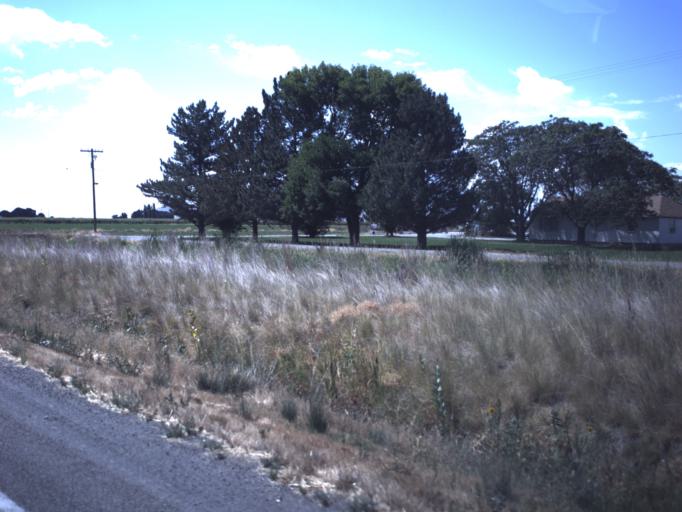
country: US
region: Utah
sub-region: Box Elder County
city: Elwood
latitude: 41.7099
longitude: -112.1422
